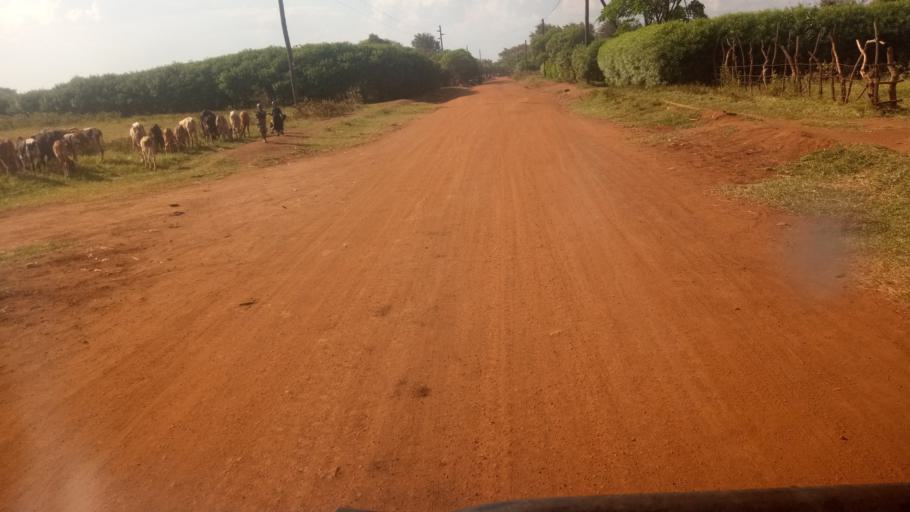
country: UG
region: Eastern Region
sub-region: Kween District
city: Binyin
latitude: 1.5077
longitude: 34.4989
